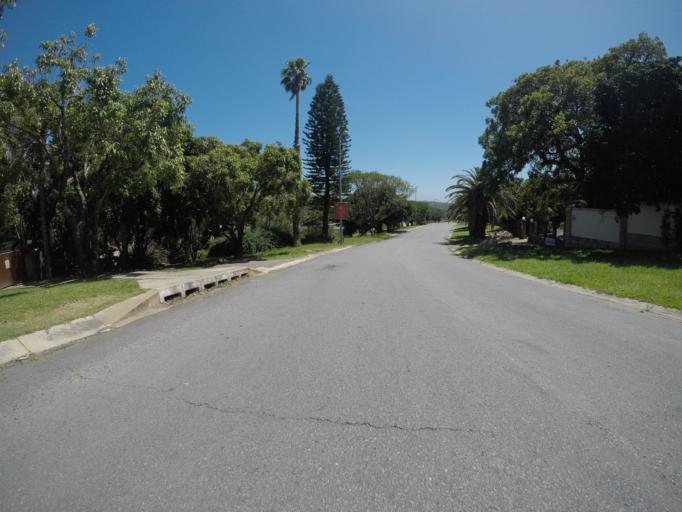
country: ZA
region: Eastern Cape
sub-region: Buffalo City Metropolitan Municipality
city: East London
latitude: -32.9656
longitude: 27.9416
